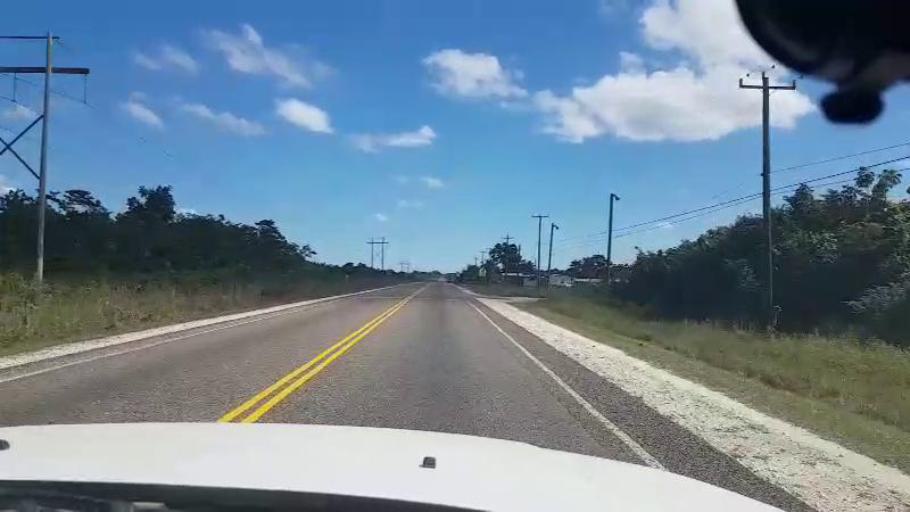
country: BZ
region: Cayo
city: Belmopan
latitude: 17.2771
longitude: -88.6486
